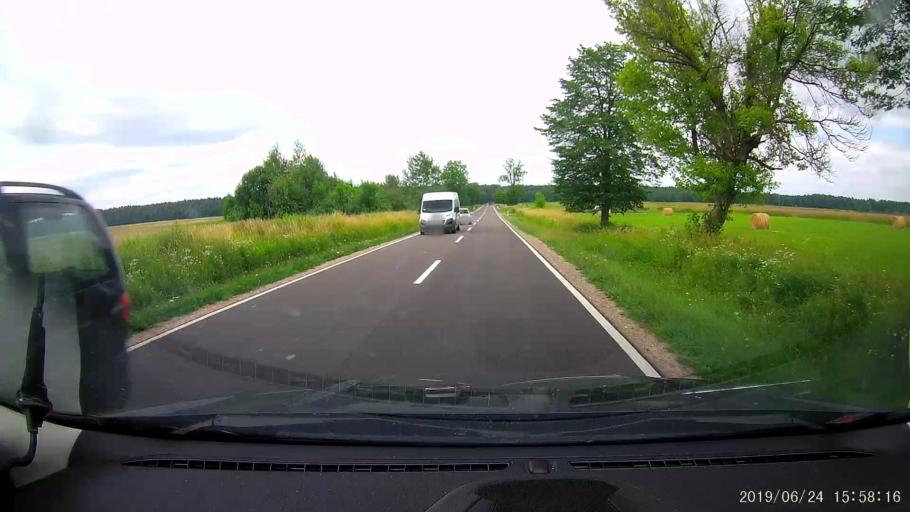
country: PL
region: Subcarpathian Voivodeship
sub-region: Powiat lubaczowski
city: Cieszanow
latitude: 50.2607
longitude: 23.1436
